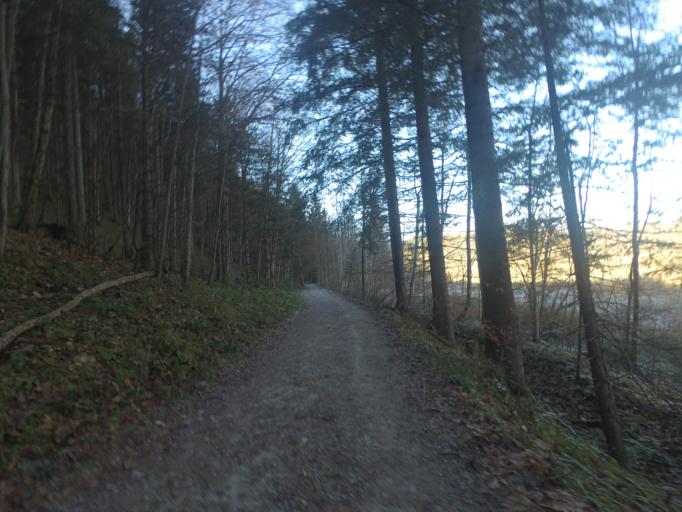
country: AT
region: Salzburg
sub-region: Politischer Bezirk Salzburg-Umgebung
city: Faistenau
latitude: 47.7512
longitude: 13.2405
